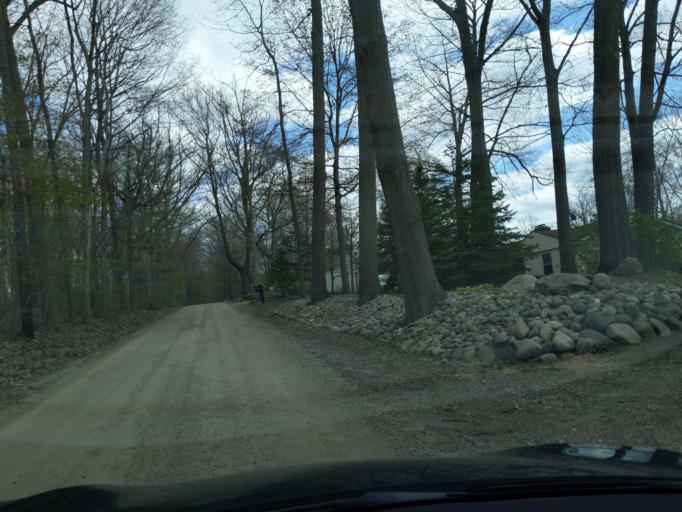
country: US
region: Michigan
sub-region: Eaton County
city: Dimondale
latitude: 42.6296
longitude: -84.6133
